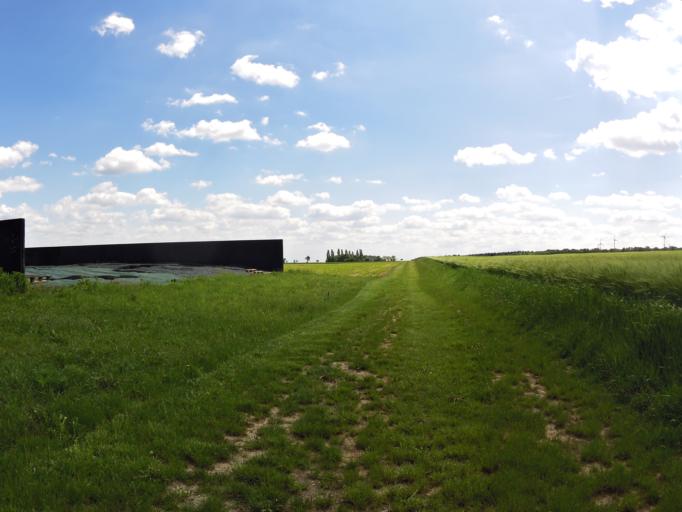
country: DE
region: Bavaria
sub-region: Regierungsbezirk Unterfranken
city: Biebelried
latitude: 49.7418
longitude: 10.0673
